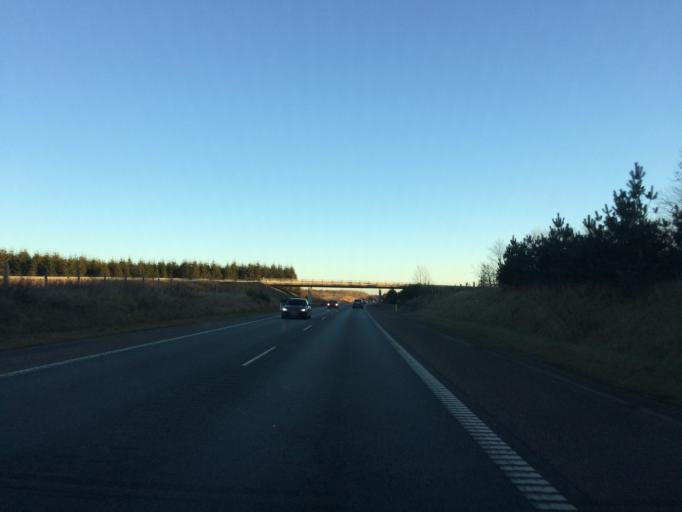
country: DK
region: Central Jutland
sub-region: Herning Kommune
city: Herning
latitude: 56.1833
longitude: 8.9661
